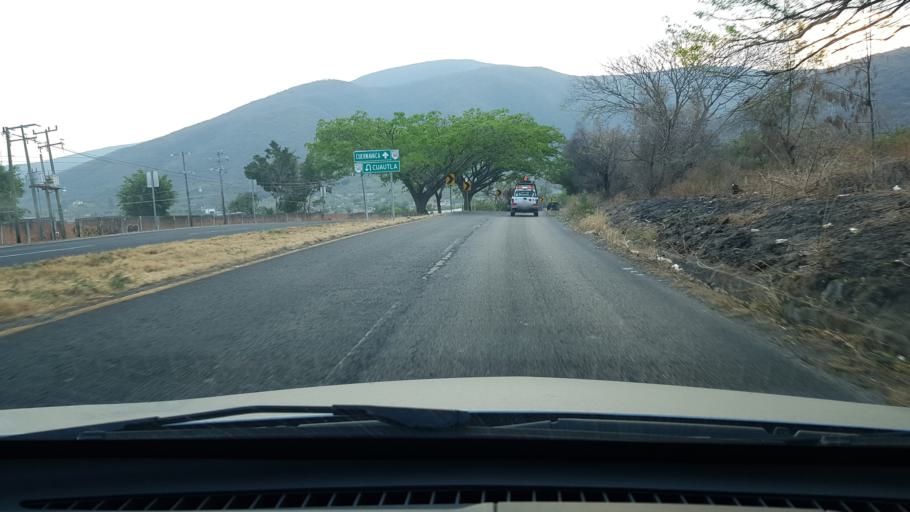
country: MX
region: Morelos
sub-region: Jiutepec
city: Independencia
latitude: 18.8593
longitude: -99.0998
